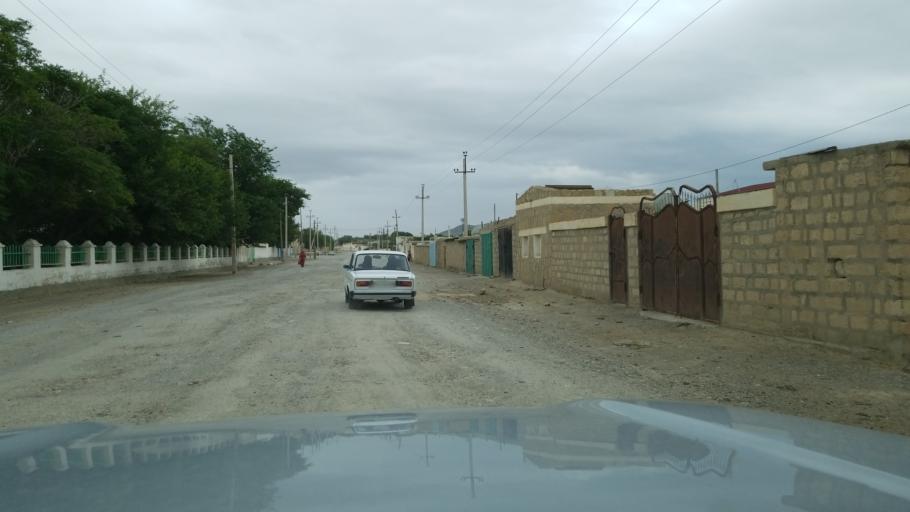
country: TM
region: Balkan
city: Serdar
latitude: 38.9822
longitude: 56.2648
